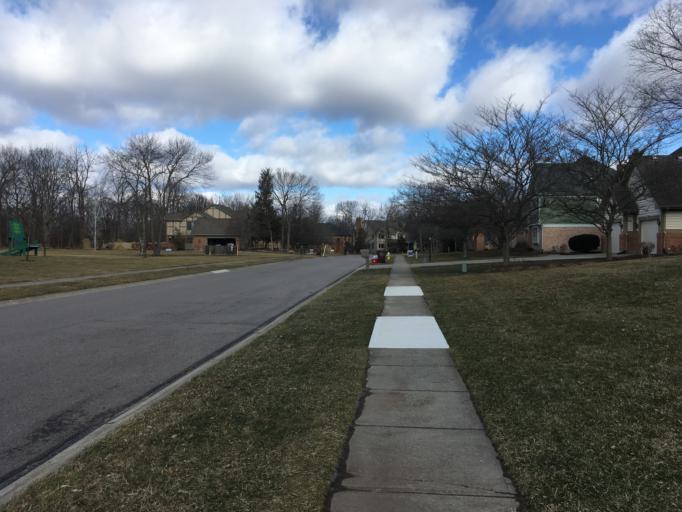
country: US
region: Ohio
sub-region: Montgomery County
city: Centerville
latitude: 39.5940
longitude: -84.1508
